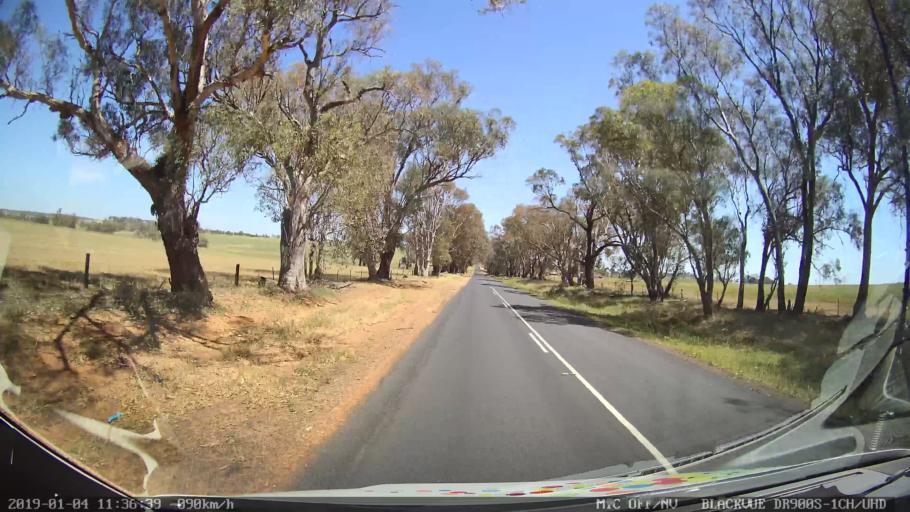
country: AU
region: New South Wales
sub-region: Cabonne
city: Molong
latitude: -33.0415
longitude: 148.8140
